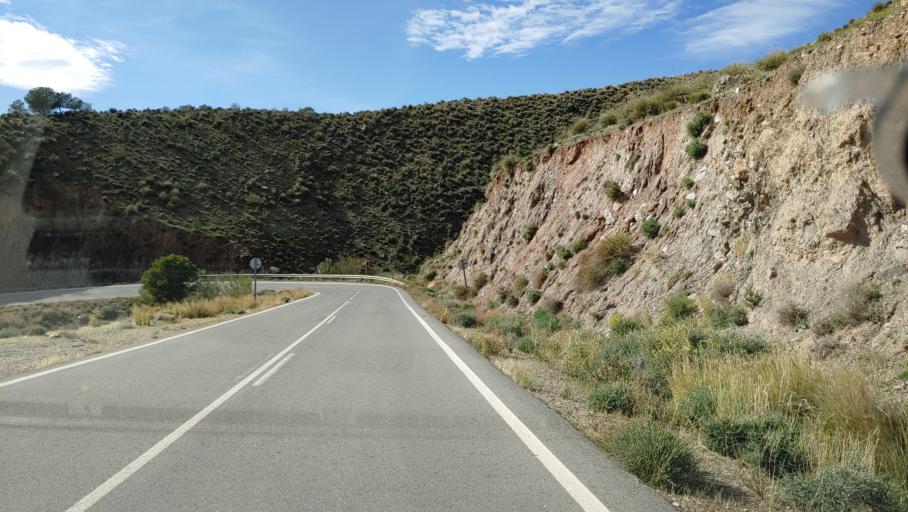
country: ES
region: Andalusia
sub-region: Provincia de Almeria
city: Canjayar
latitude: 37.0224
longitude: -2.7274
